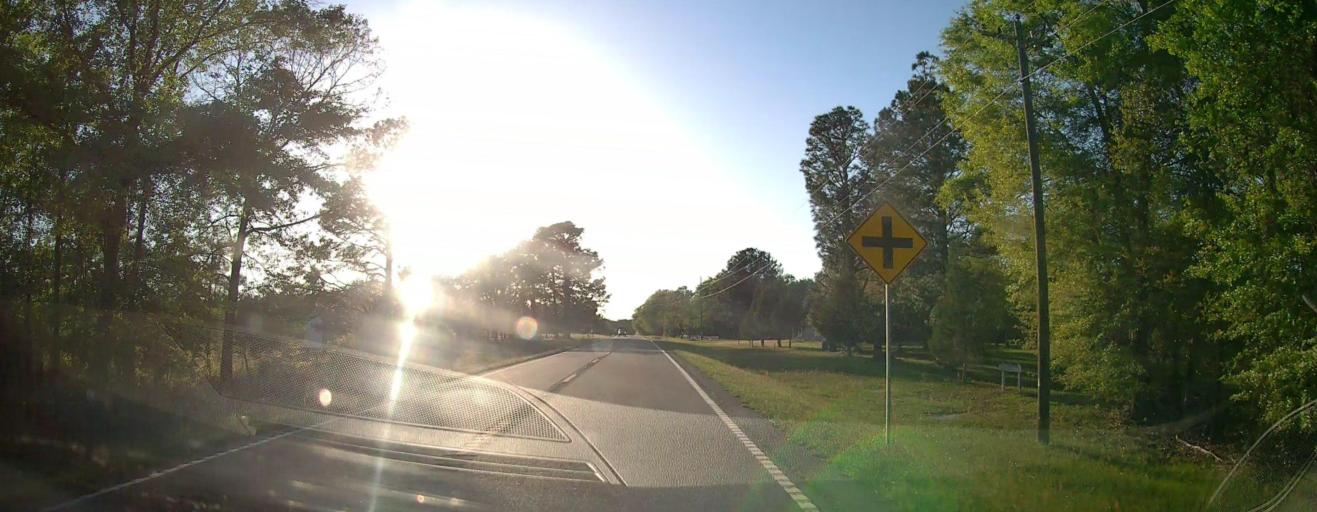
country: US
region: Georgia
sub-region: Schley County
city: Ellaville
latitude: 32.3311
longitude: -84.3409
